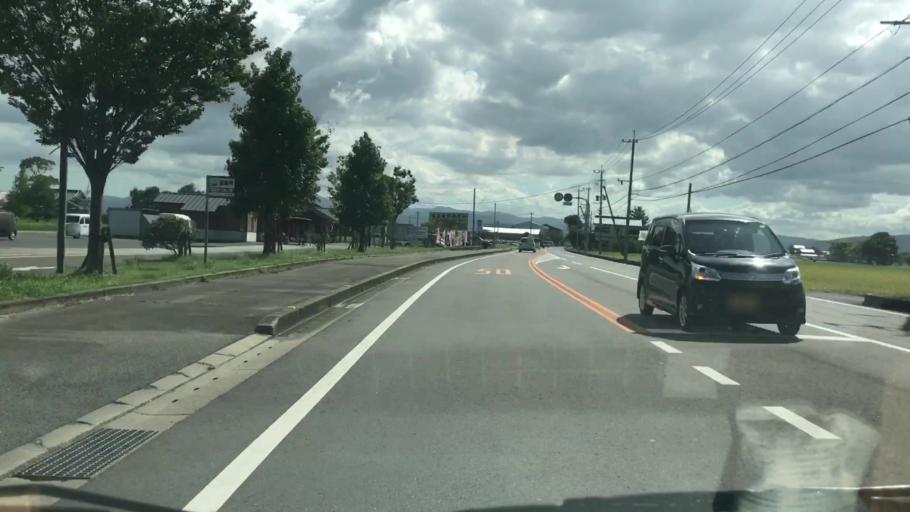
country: JP
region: Saga Prefecture
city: Kashima
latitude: 33.1806
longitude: 130.1888
